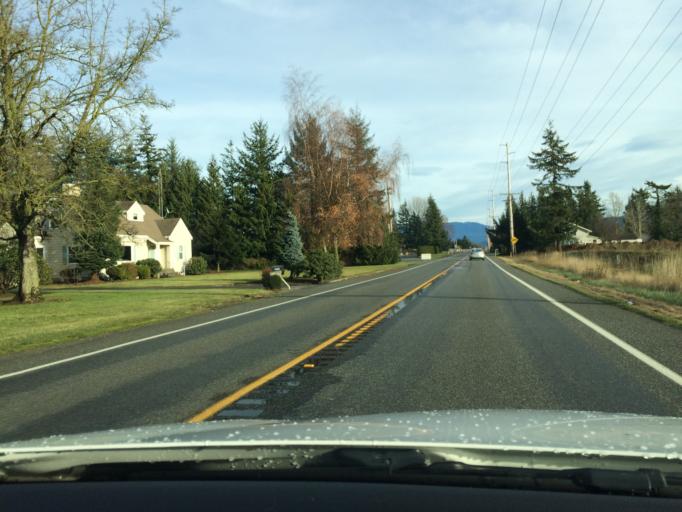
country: US
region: Washington
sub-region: Whatcom County
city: Lynden
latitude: 48.9641
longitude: -122.4127
